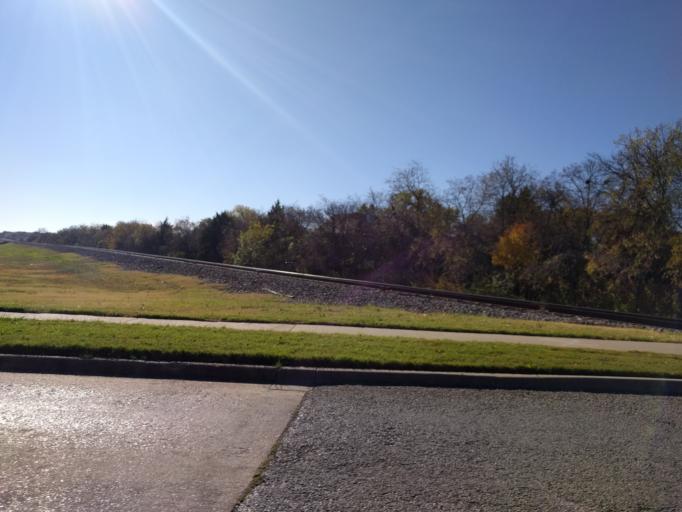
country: US
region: Texas
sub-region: Dallas County
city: Richardson
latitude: 32.9754
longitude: -96.7291
